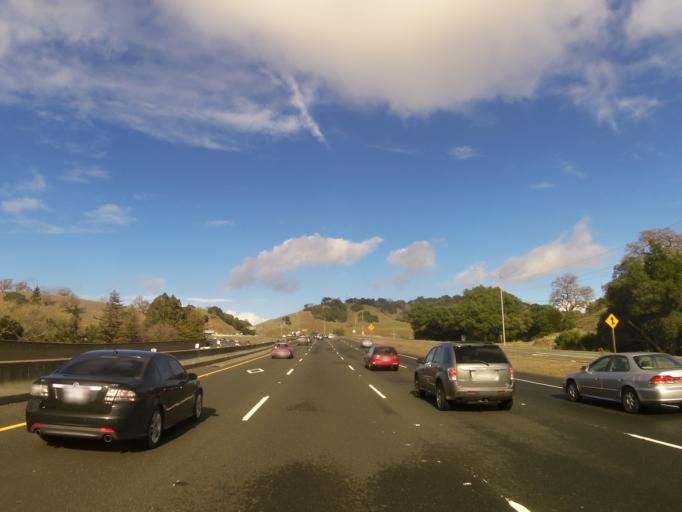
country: US
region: California
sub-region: Marin County
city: Santa Venetia
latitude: 38.0346
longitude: -122.5368
